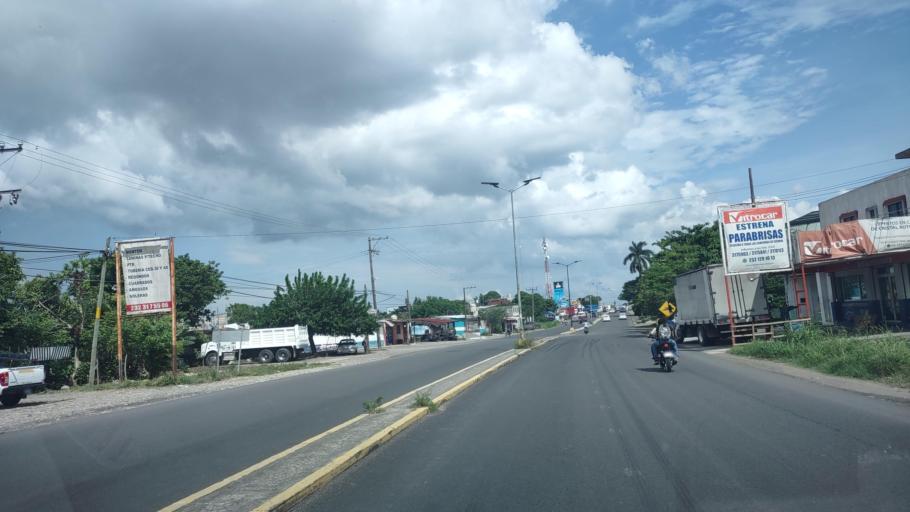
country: MX
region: Veracruz
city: Martinez de la Torre
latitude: 20.0720
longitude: -97.0673
